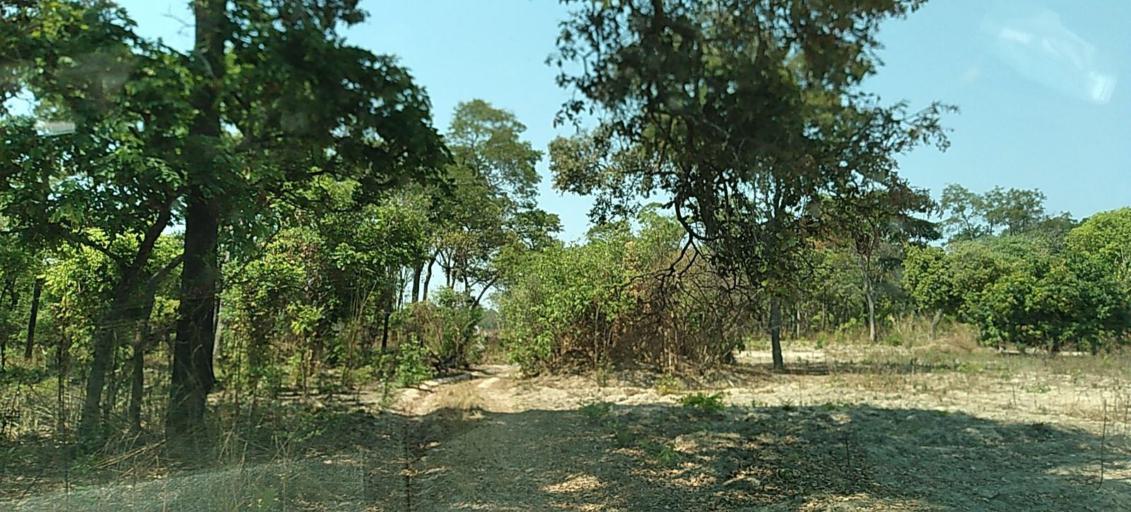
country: ZM
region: Copperbelt
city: Mpongwe
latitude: -13.7887
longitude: 28.0983
